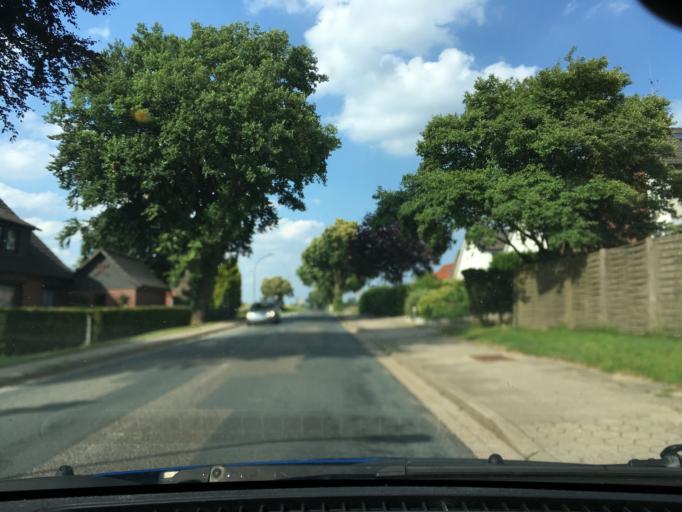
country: DE
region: Lower Saxony
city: Bendestorf
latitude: 53.3712
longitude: 9.9401
